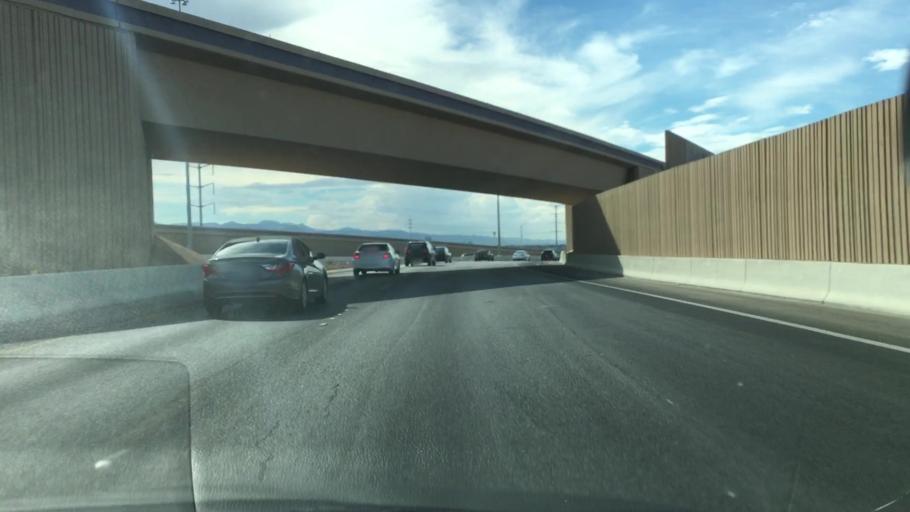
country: US
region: Nevada
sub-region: Clark County
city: Whitney
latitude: 36.0660
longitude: -115.0323
